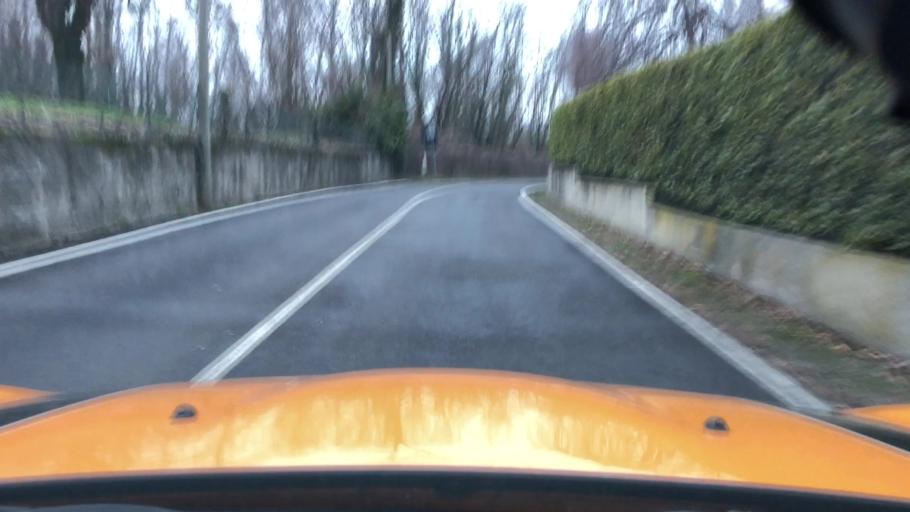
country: IT
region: Lombardy
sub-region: Provincia di Como
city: Senna Comasco
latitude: 45.7559
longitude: 9.1161
